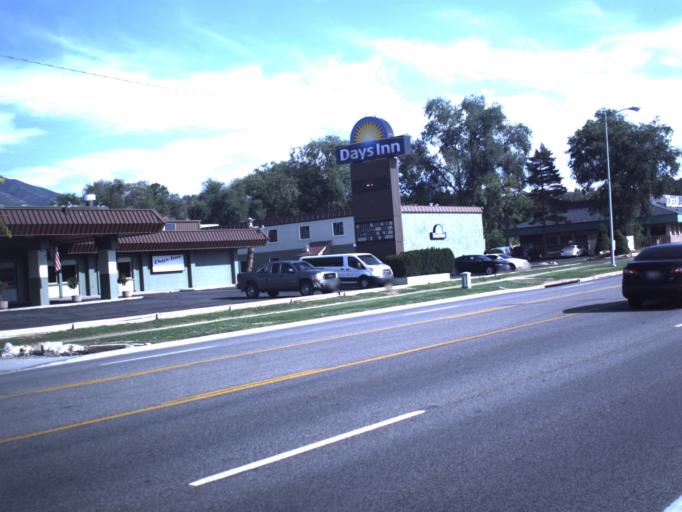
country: US
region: Utah
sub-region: Weber County
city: South Ogden
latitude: 41.2038
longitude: -111.9710
